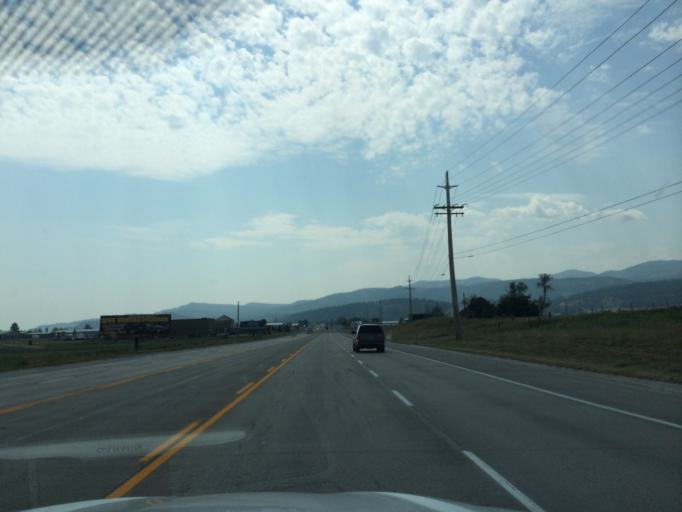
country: US
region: Montana
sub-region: Flathead County
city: Kalispell
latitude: 48.1614
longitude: -114.2879
